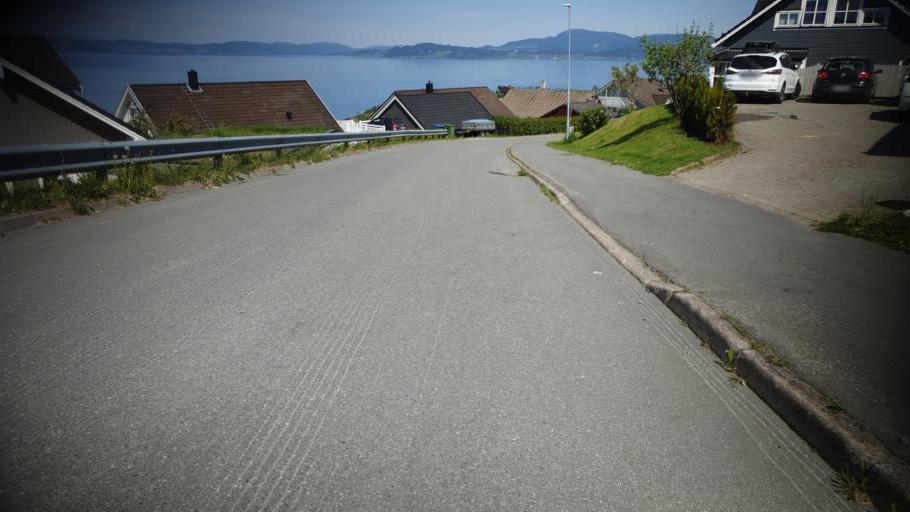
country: NO
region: Sor-Trondelag
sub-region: Malvik
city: Malvik
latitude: 63.4345
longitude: 10.6212
